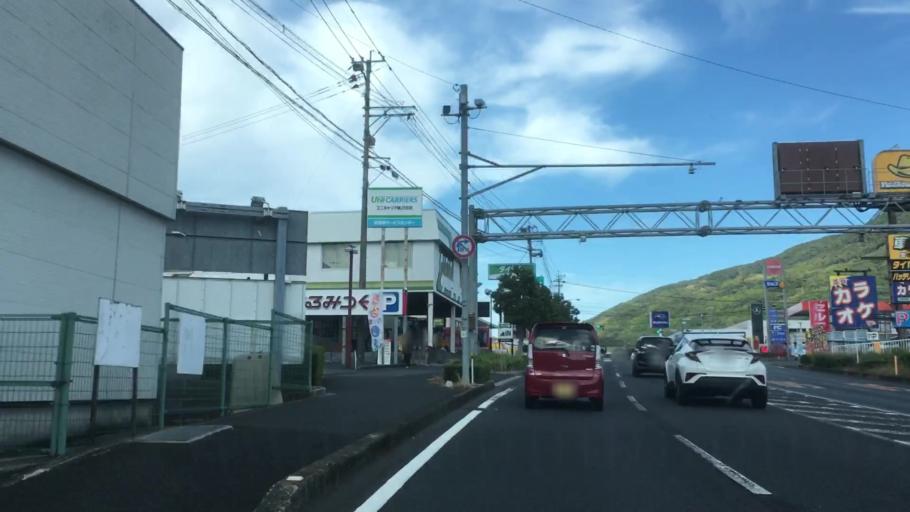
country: JP
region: Nagasaki
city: Sasebo
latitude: 33.1568
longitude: 129.7672
